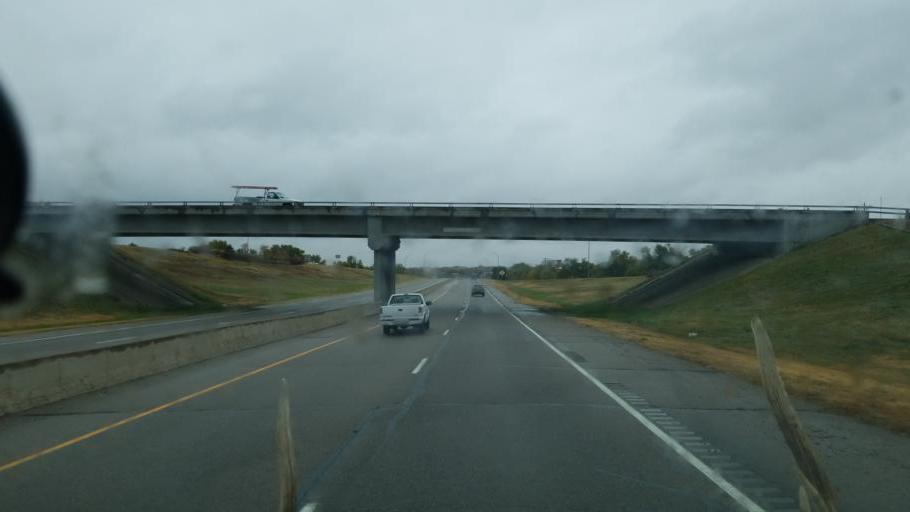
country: US
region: Colorado
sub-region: Pueblo County
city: Pueblo
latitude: 38.2752
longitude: -104.5589
